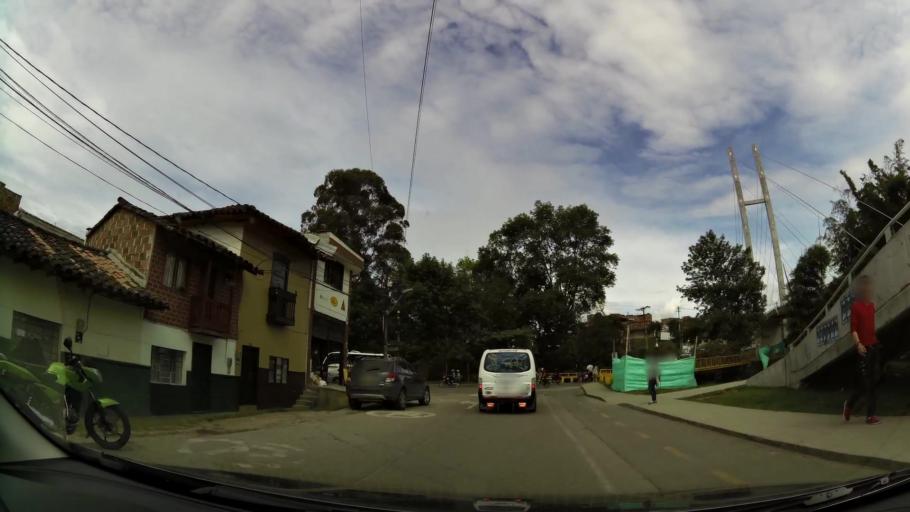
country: CO
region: Antioquia
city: Rionegro
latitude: 6.1555
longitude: -75.3682
